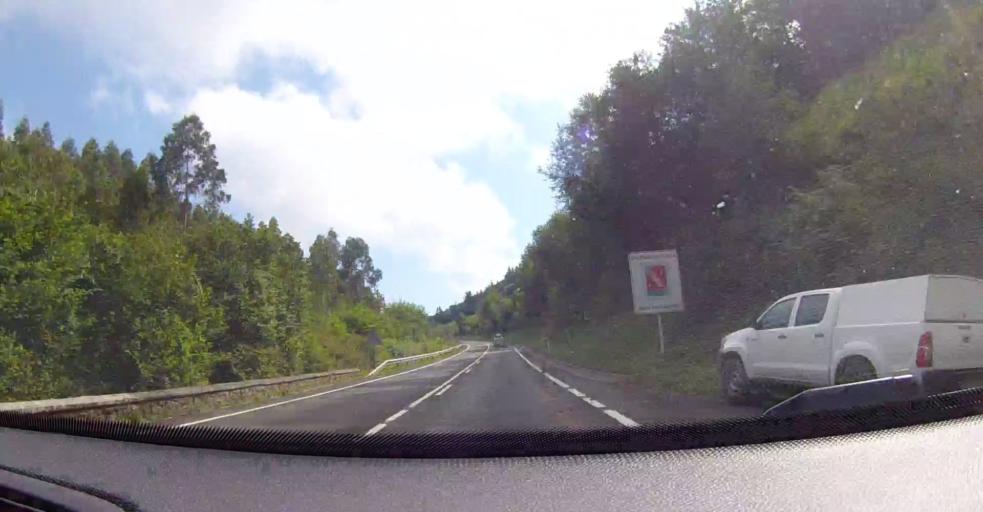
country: ES
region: Basque Country
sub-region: Bizkaia
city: Ibarrangelu
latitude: 43.3744
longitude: -2.6365
